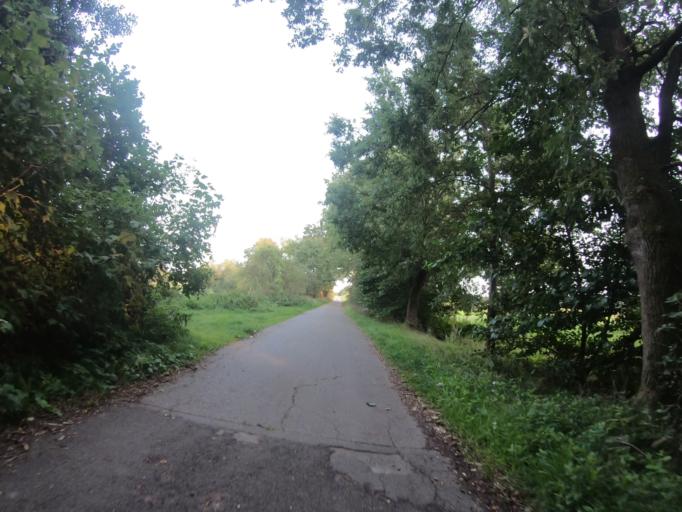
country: DE
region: Lower Saxony
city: Leiferde
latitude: 52.4334
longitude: 10.4527
